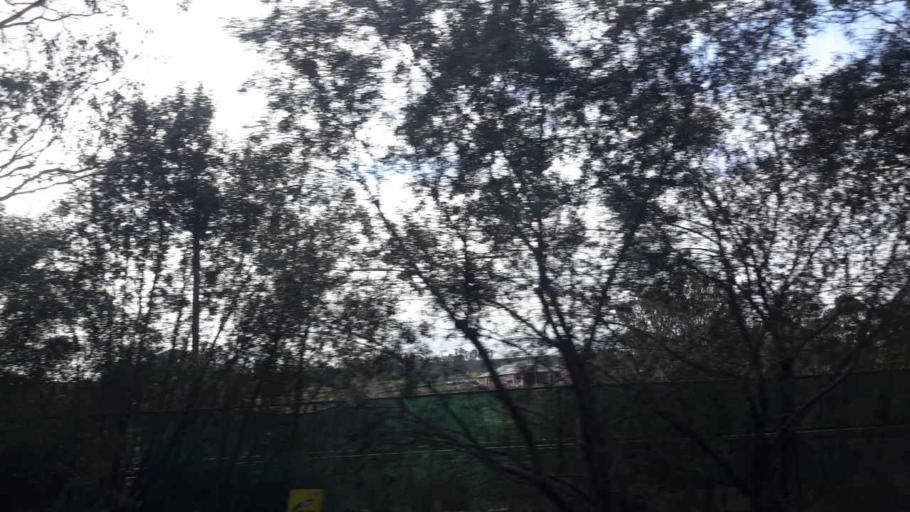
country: AU
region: New South Wales
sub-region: Campbelltown Municipality
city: Glen Alpine
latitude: -34.0798
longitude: 150.7817
